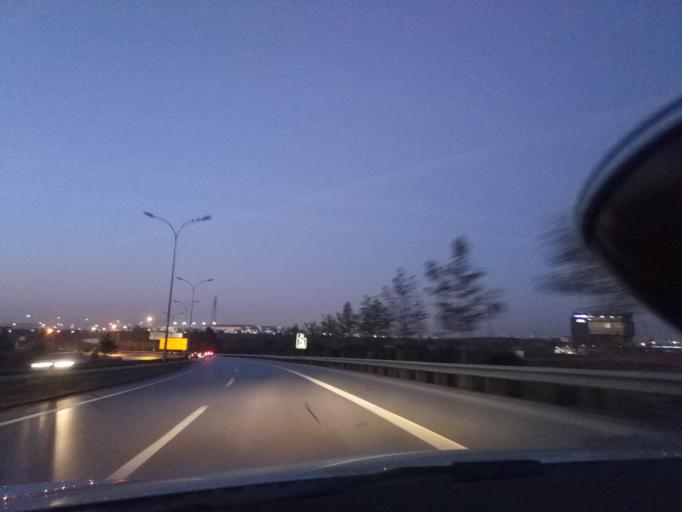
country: TR
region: Istanbul
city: Sultanbeyli
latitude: 40.9216
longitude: 29.3219
